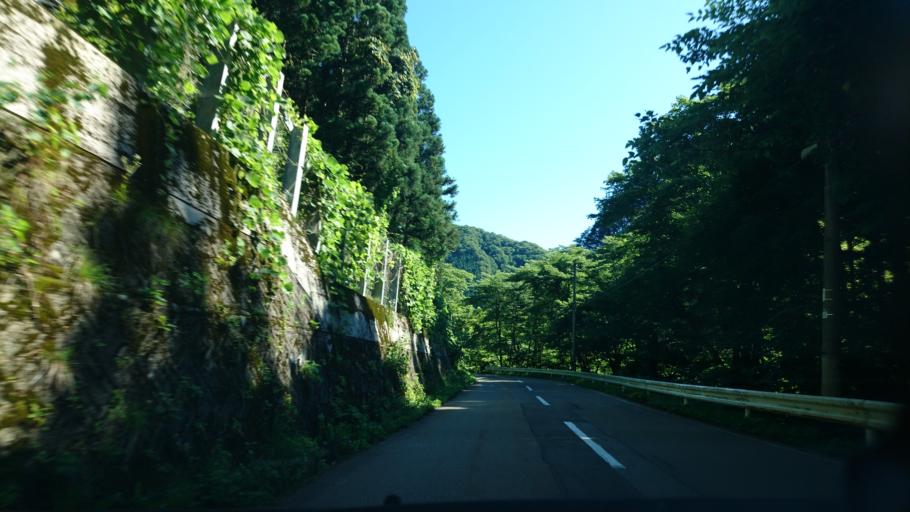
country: JP
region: Akita
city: Kakunodatemachi
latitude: 39.7127
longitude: 140.6180
